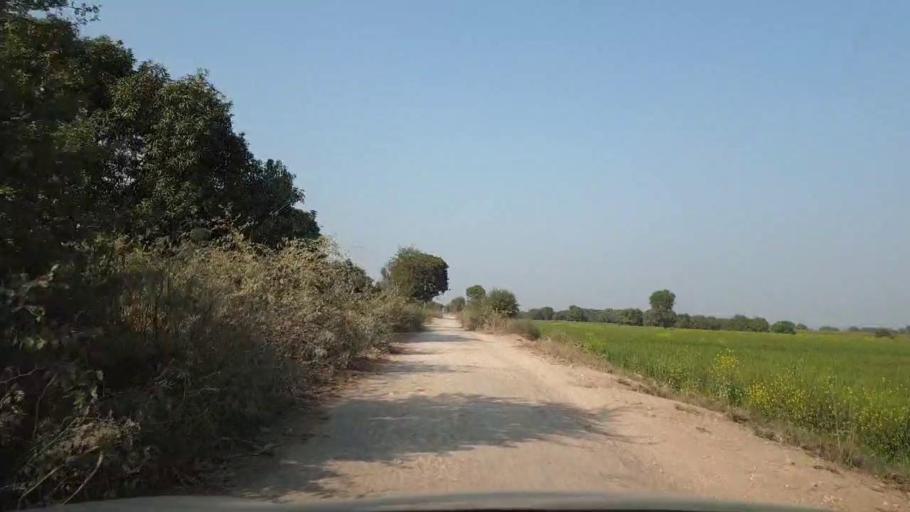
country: PK
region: Sindh
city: Tando Allahyar
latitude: 25.5594
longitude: 68.7940
